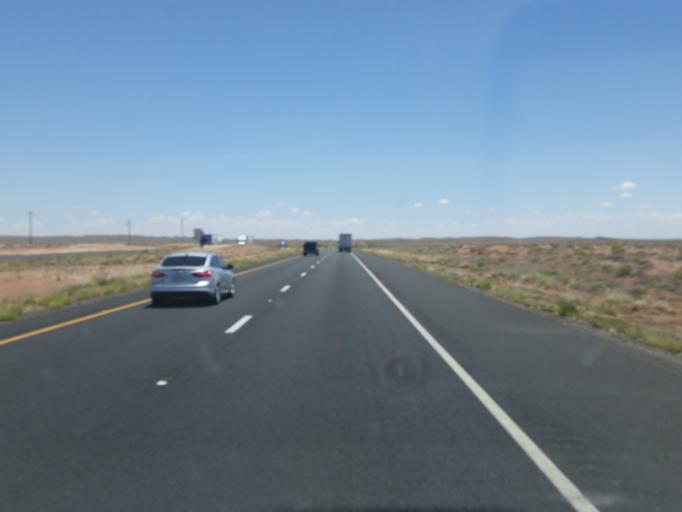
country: US
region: Arizona
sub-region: Coconino County
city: LeChee
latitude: 35.0573
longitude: -110.8013
